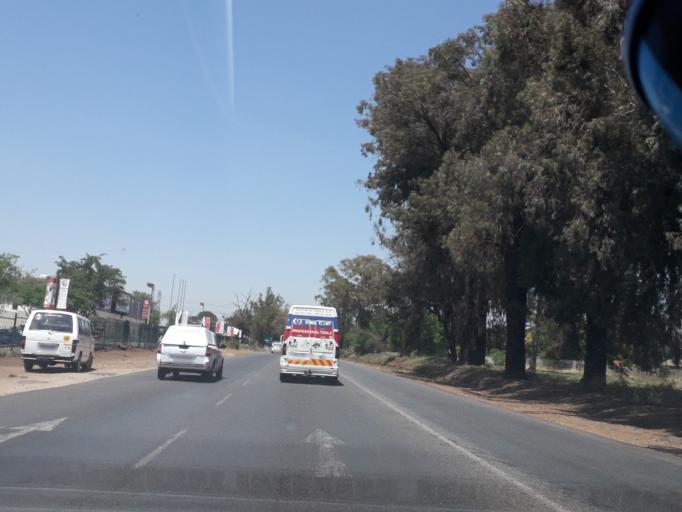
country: ZA
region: Gauteng
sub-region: City of Tshwane Metropolitan Municipality
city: Centurion
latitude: -25.8865
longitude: 28.1609
